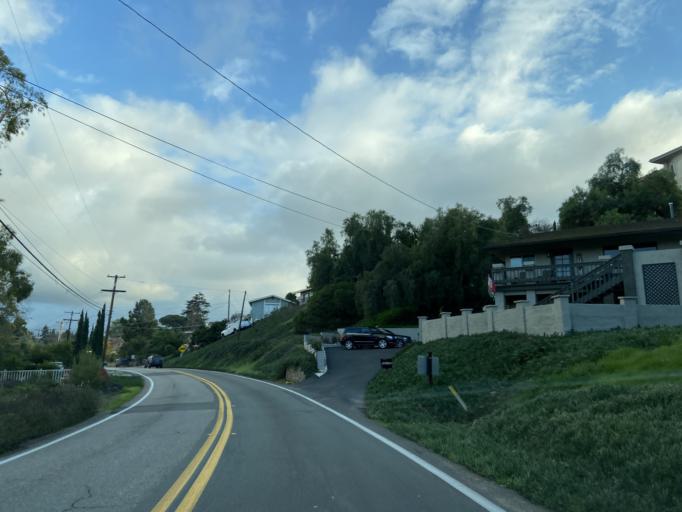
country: US
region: California
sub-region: San Diego County
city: Casa de Oro-Mount Helix
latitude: 32.7719
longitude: -116.9783
